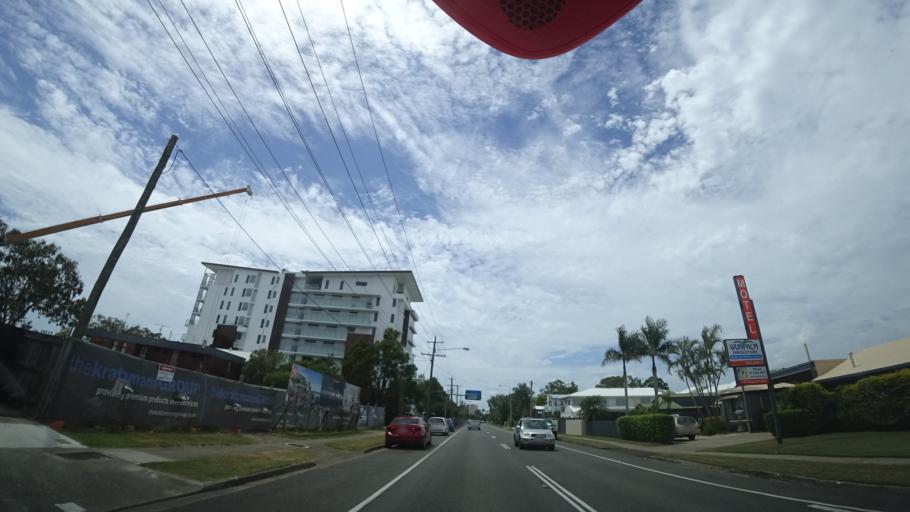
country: AU
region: Queensland
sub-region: Sunshine Coast
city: Buderim
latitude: -26.6448
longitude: 153.0851
